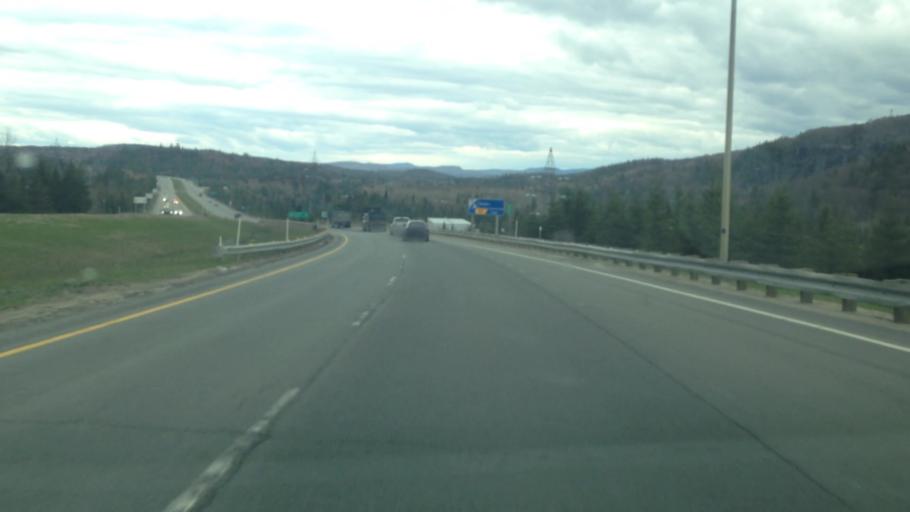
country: CA
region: Quebec
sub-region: Laurentides
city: Sainte-Agathe-des-Monts
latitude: 46.0476
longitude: -74.2659
